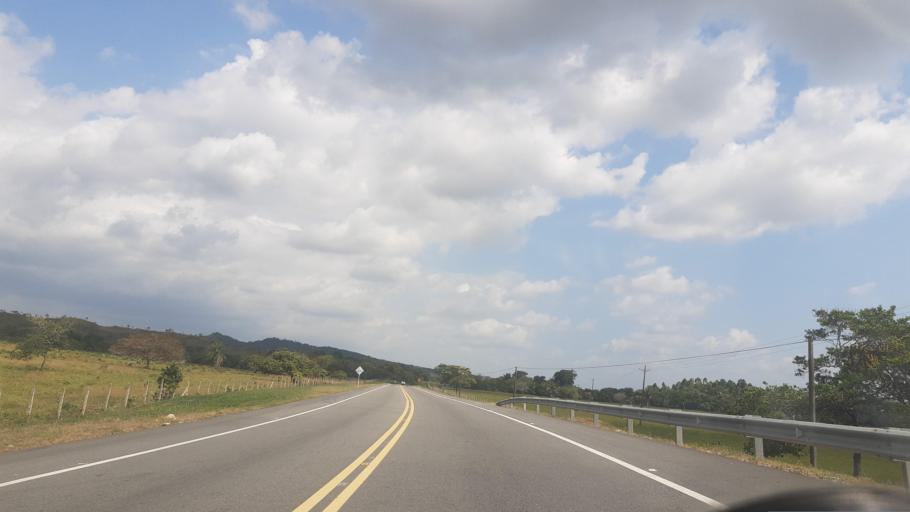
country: CO
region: Casanare
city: Tauramena
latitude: 4.8474
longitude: -72.7231
